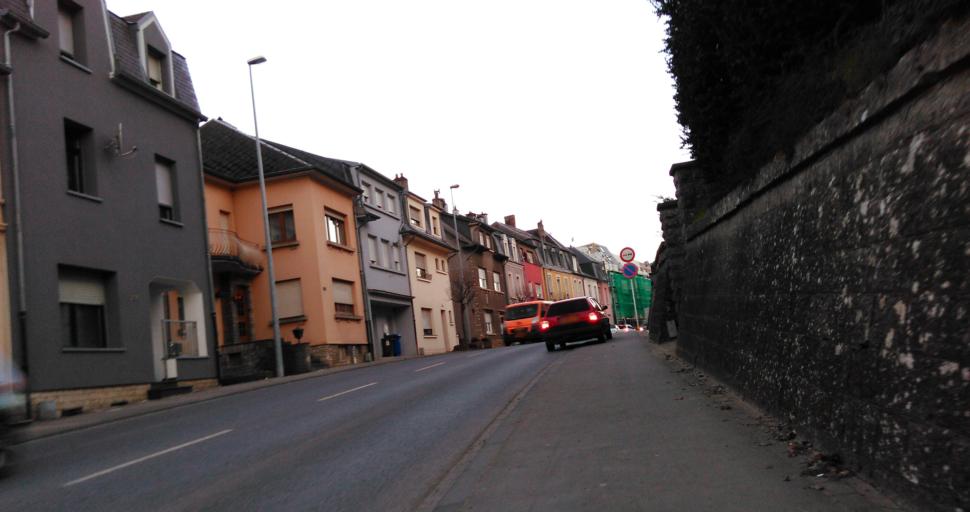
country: LU
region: Luxembourg
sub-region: Canton d'Esch-sur-Alzette
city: Niedercorn
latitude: 49.5328
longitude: 5.8913
